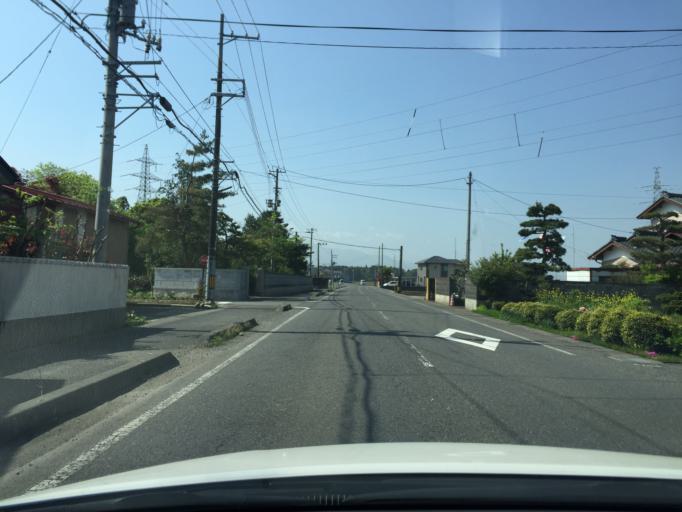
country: JP
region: Niigata
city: Gosen
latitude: 37.7463
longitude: 139.2036
